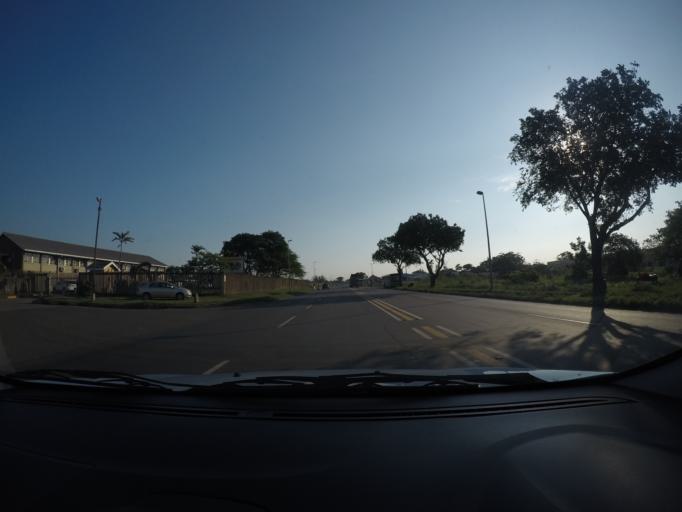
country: ZA
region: KwaZulu-Natal
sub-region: uThungulu District Municipality
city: Richards Bay
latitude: -28.7586
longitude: 32.0242
